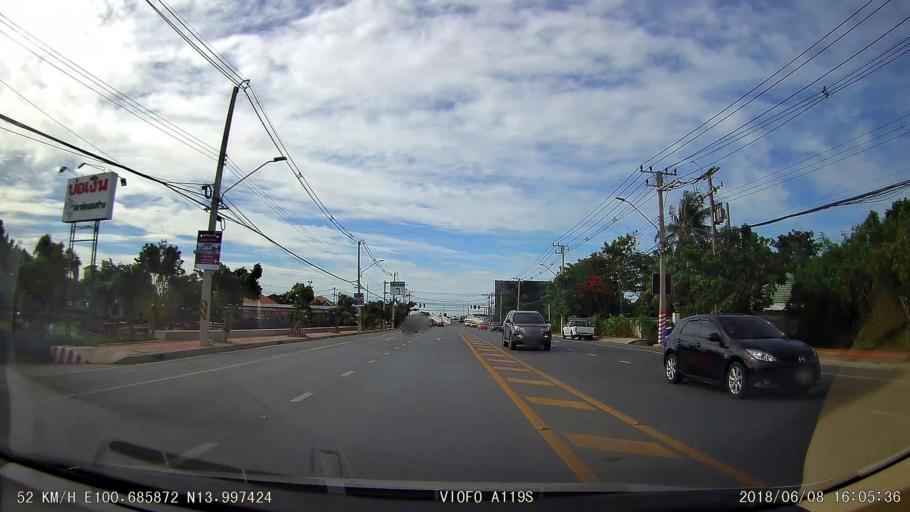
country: TH
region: Pathum Thani
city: Thanyaburi
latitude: 13.9976
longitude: 100.6859
